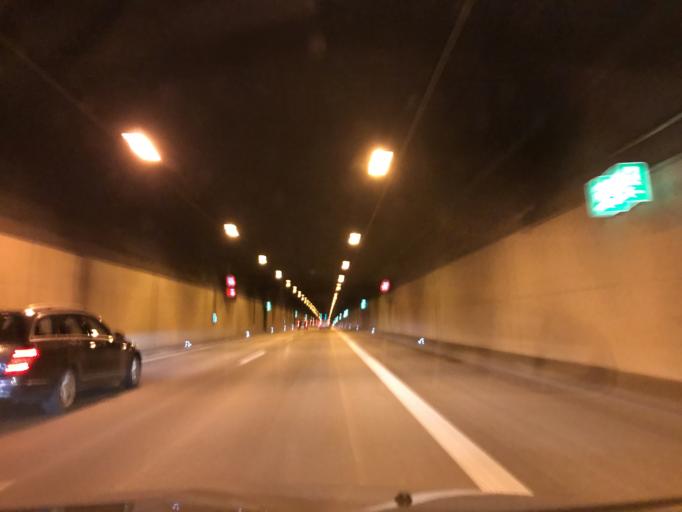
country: DE
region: Baden-Wuerttemberg
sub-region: Regierungsbezirk Stuttgart
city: Fellbach
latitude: 48.8007
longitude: 9.2790
